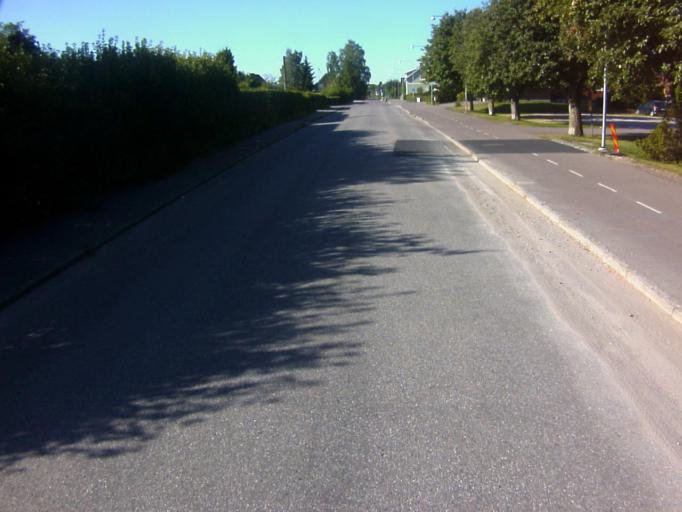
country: SE
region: Soedermanland
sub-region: Eskilstuna Kommun
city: Eskilstuna
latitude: 59.3824
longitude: 16.5326
